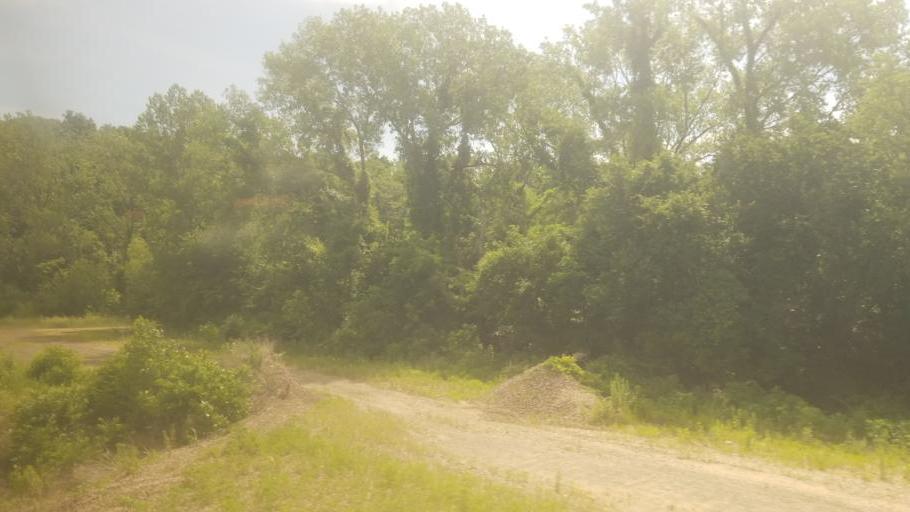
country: US
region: Missouri
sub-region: Jackson County
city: East Independence
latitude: 39.1590
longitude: -94.3659
